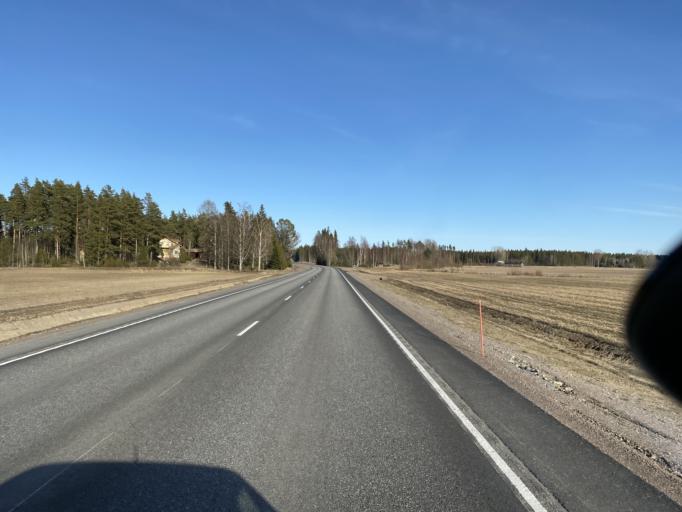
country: FI
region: Satakunta
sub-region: Rauma
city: Koeylioe
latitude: 61.1627
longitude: 22.3235
